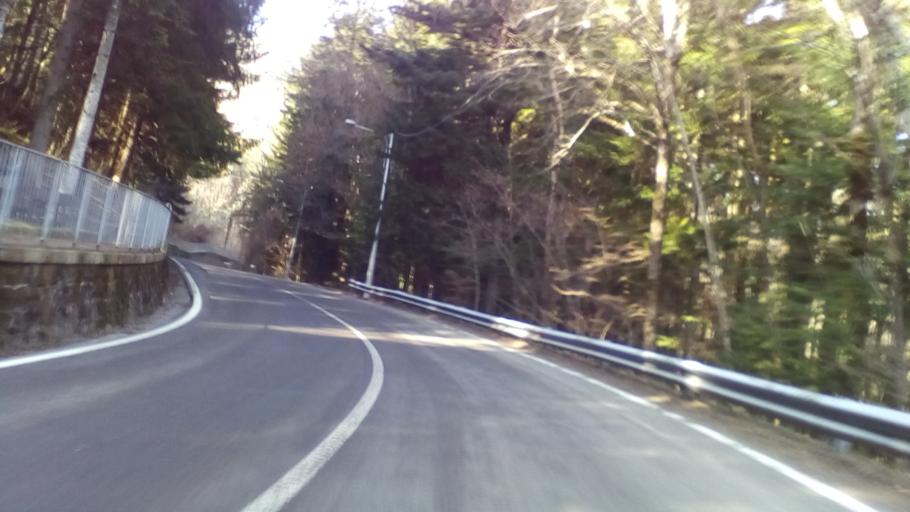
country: IT
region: Emilia-Romagna
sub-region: Provincia di Modena
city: Pievepelago
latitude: 44.2082
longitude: 10.6124
